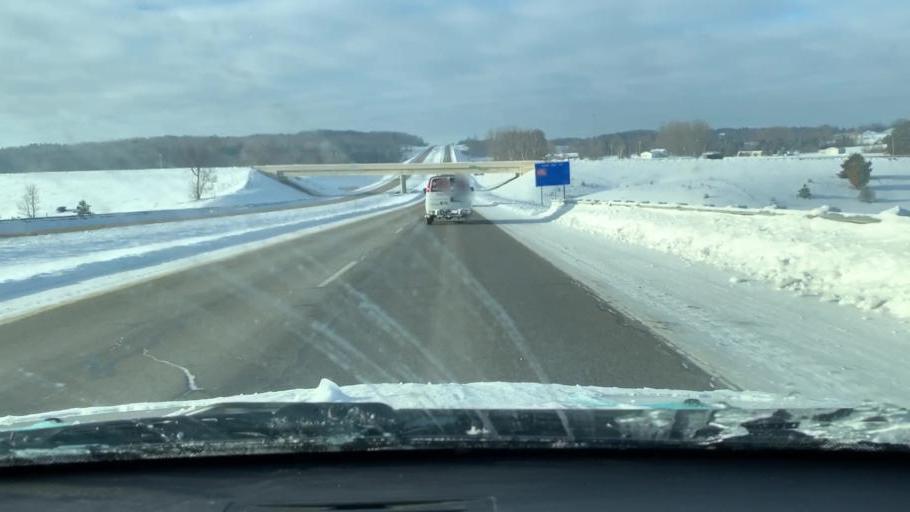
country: US
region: Michigan
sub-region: Wexford County
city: Cadillac
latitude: 44.2332
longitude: -85.3771
